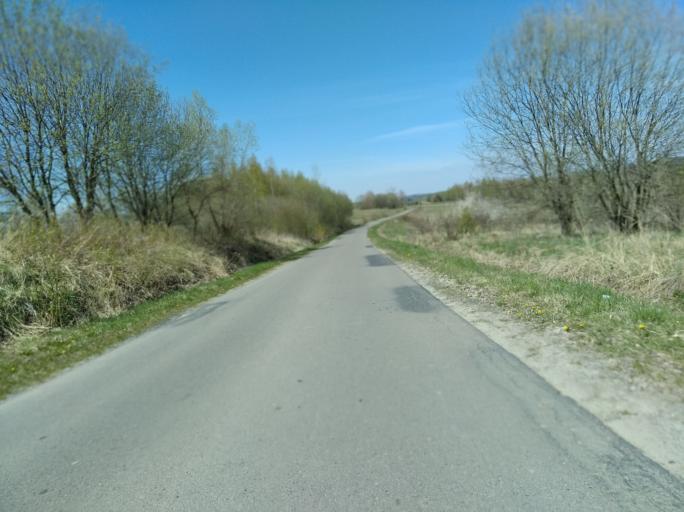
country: PL
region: Subcarpathian Voivodeship
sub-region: Powiat brzozowski
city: Jablonka
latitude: 49.7361
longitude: 22.1153
